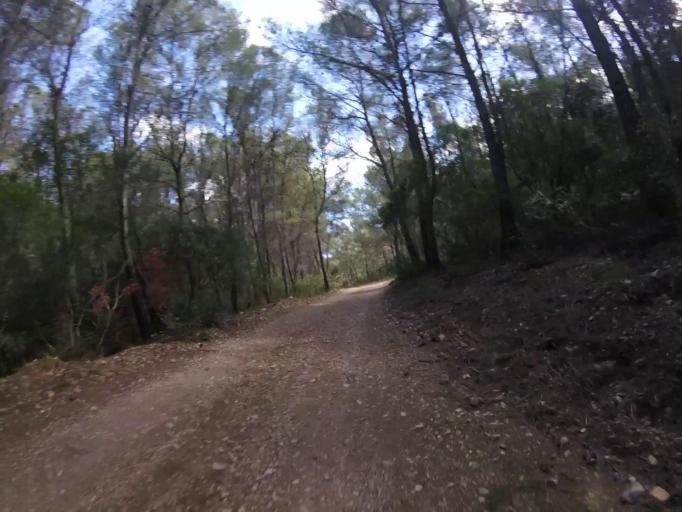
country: ES
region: Valencia
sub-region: Provincia de Castello
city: Alcoceber
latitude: 40.2974
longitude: 0.3142
